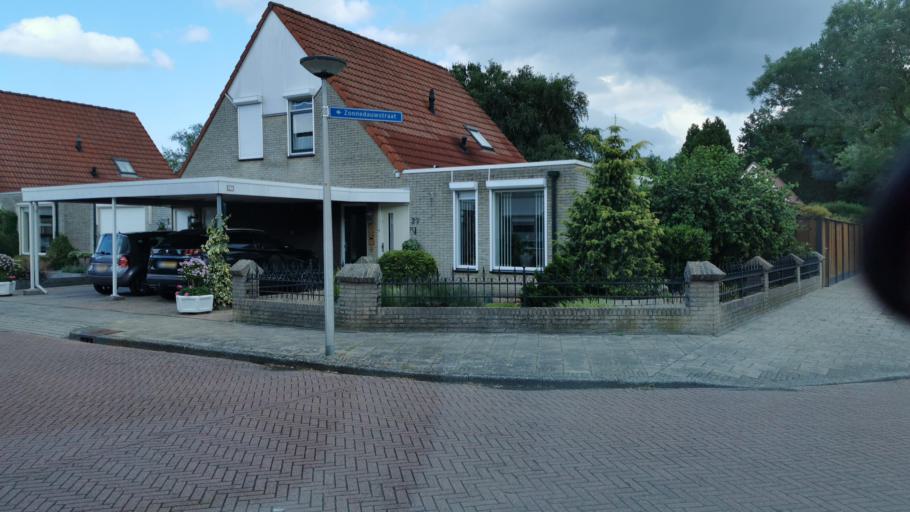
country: DE
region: North Rhine-Westphalia
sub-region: Regierungsbezirk Munster
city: Gronau
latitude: 52.2181
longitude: 6.9685
